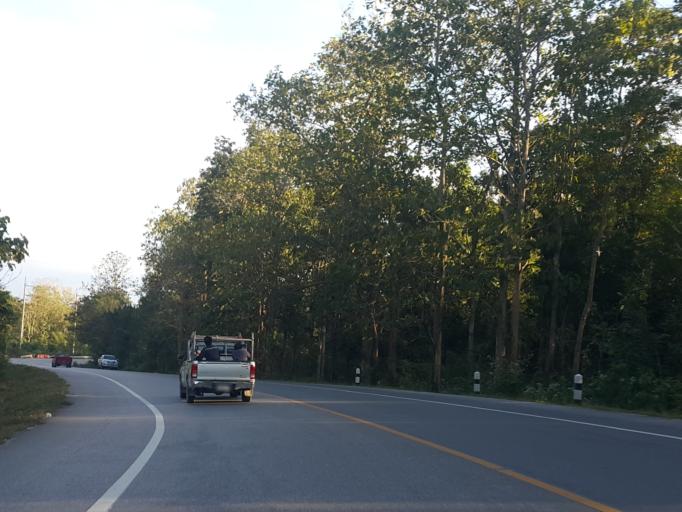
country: TH
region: Lampang
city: Lampang
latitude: 18.4807
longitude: 99.5492
